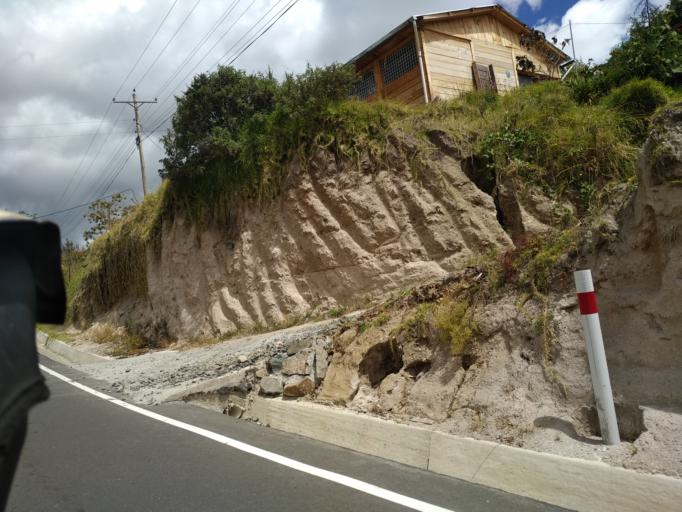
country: EC
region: Cotopaxi
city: Saquisili
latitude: -0.7899
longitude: -78.9128
